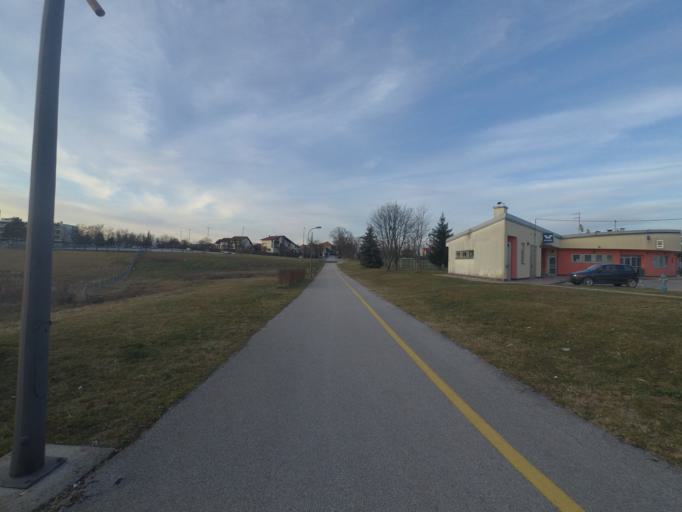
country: HR
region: Karlovacka
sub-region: Grad Karlovac
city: Karlovac
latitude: 45.4752
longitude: 15.5421
